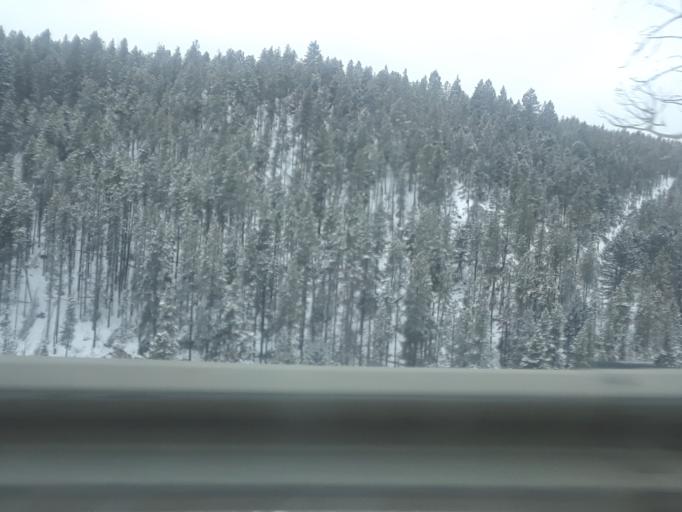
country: US
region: Colorado
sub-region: Boulder County
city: Coal Creek
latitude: 39.9241
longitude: -105.4196
